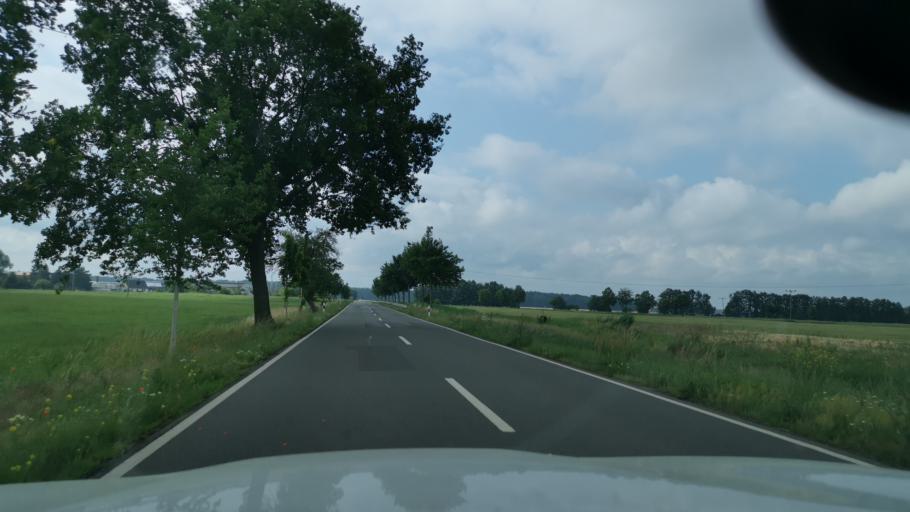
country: DE
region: Saxony-Anhalt
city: Annaburg
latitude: 51.7664
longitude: 13.0301
